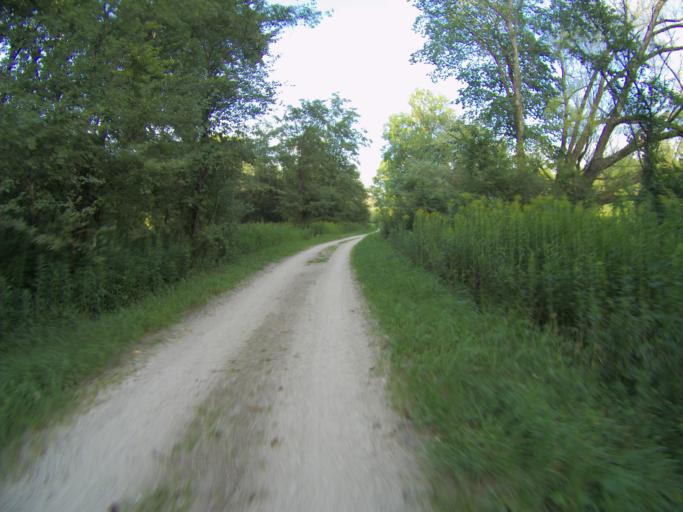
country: DE
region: Bavaria
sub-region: Upper Bavaria
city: Hallbergmoos
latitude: 48.3302
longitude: 11.7092
